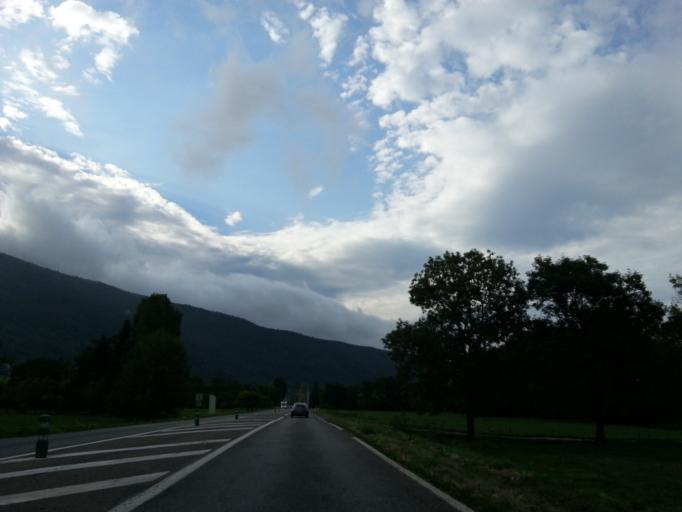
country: FR
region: Rhone-Alpes
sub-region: Departement de la Haute-Savoie
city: Saint-Jorioz
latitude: 45.8393
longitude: 6.1565
